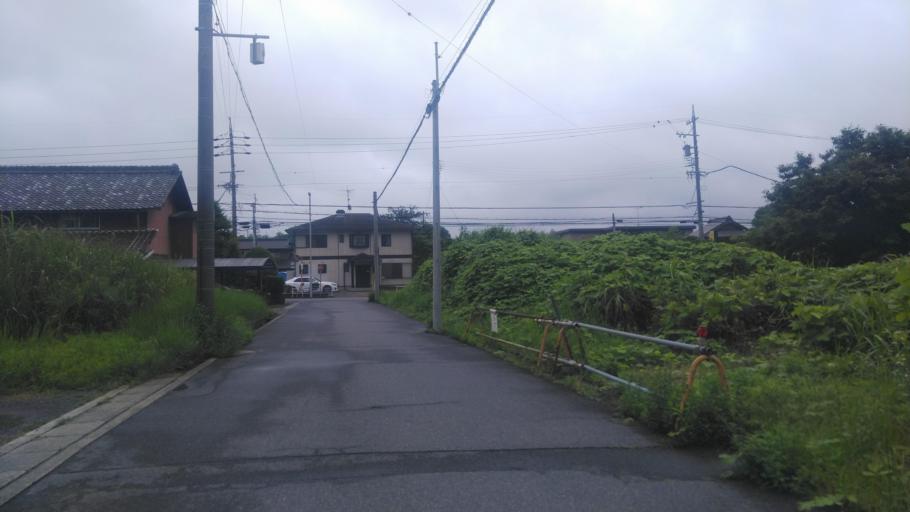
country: JP
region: Aichi
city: Kasugai
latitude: 35.2461
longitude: 137.0272
